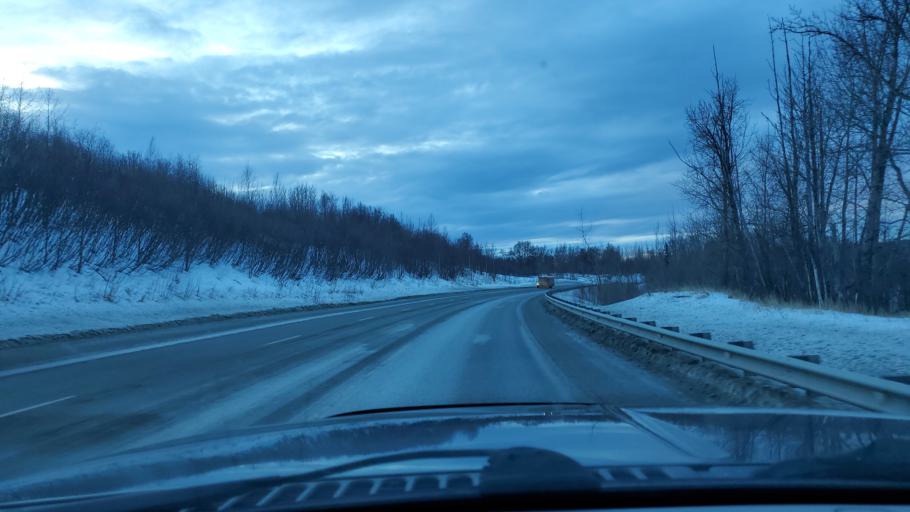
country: US
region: Alaska
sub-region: Matanuska-Susitna Borough
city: Lazy Mountain
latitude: 61.6789
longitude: -148.9926
